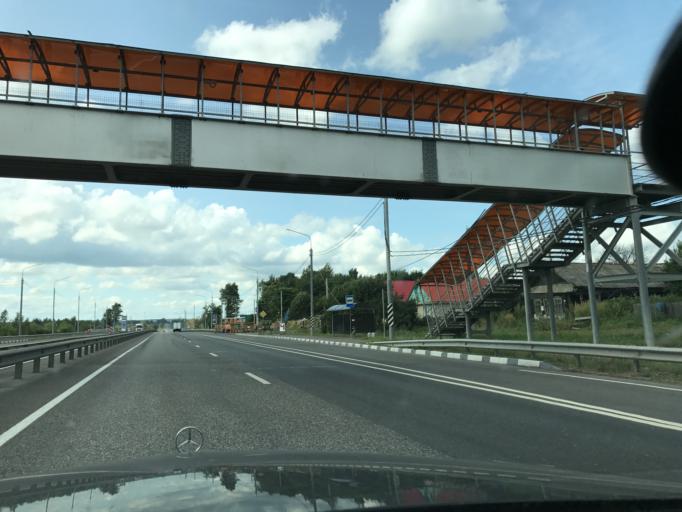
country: RU
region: Vladimir
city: Gorokhovets
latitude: 56.1660
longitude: 42.4772
